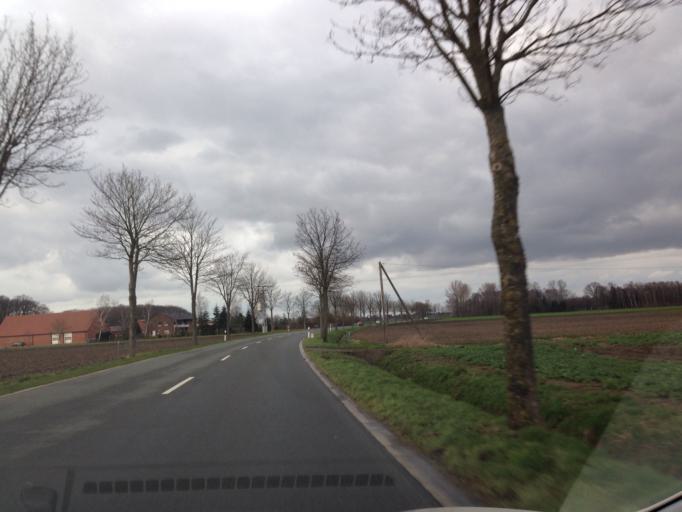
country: DE
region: North Rhine-Westphalia
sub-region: Regierungsbezirk Munster
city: Senden
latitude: 51.8017
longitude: 7.5360
